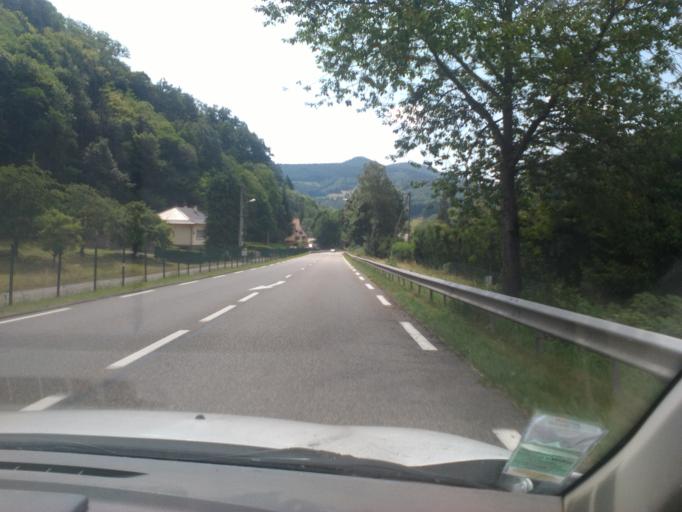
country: FR
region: Alsace
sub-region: Departement du Haut-Rhin
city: Lapoutroie
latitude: 48.1551
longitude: 7.1692
